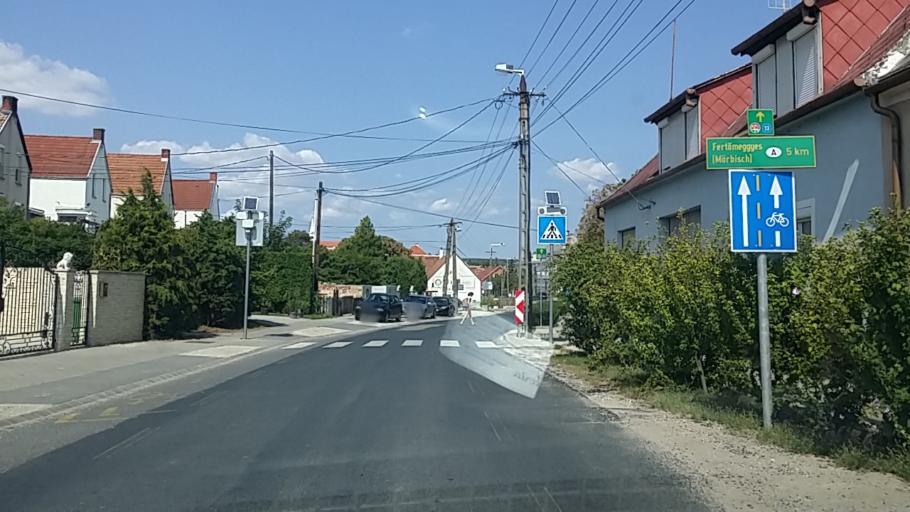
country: HU
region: Gyor-Moson-Sopron
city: Fertorakos
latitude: 47.7135
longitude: 16.6560
